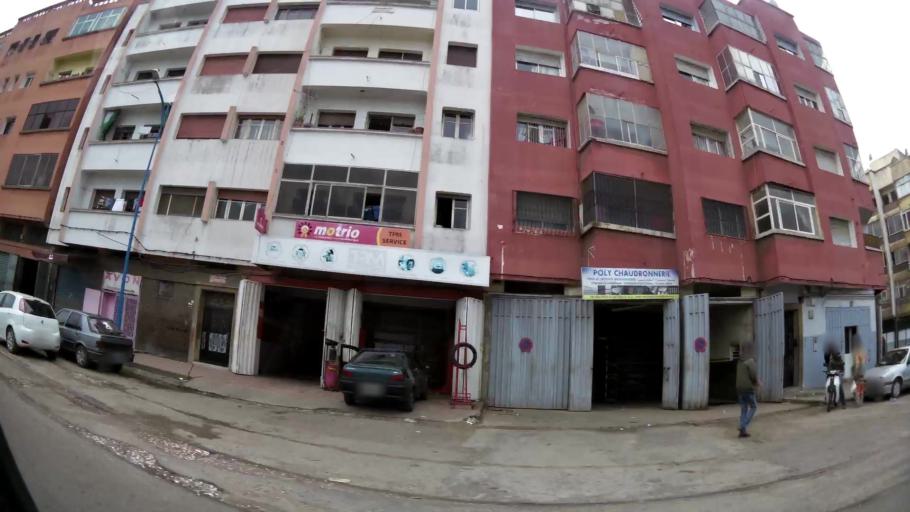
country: MA
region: Grand Casablanca
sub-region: Casablanca
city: Casablanca
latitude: 33.5953
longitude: -7.5575
